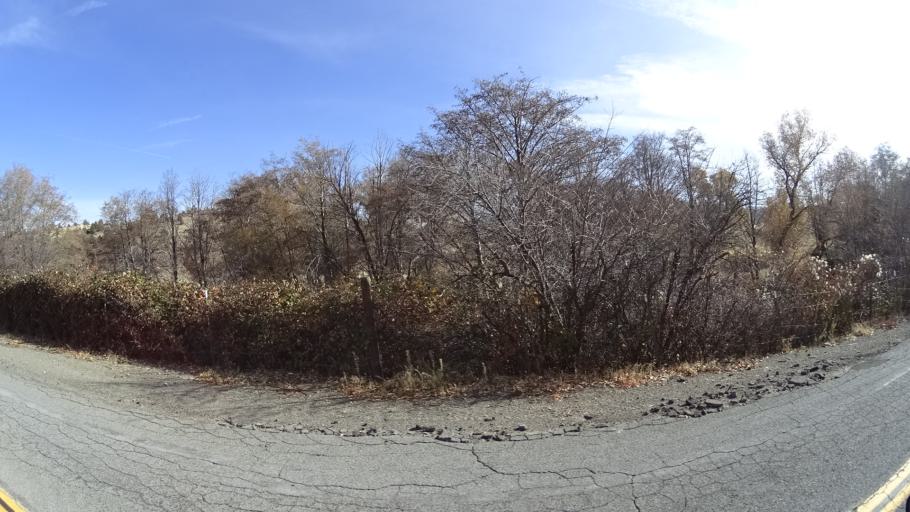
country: US
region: California
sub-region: Siskiyou County
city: Weed
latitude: 41.4749
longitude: -122.4406
